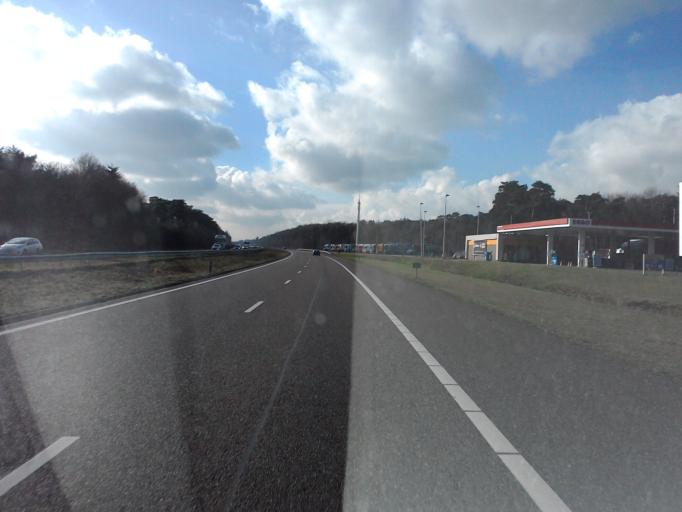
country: NL
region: North Brabant
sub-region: Gemeente Veldhoven
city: Oerle
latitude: 51.3956
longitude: 5.3825
